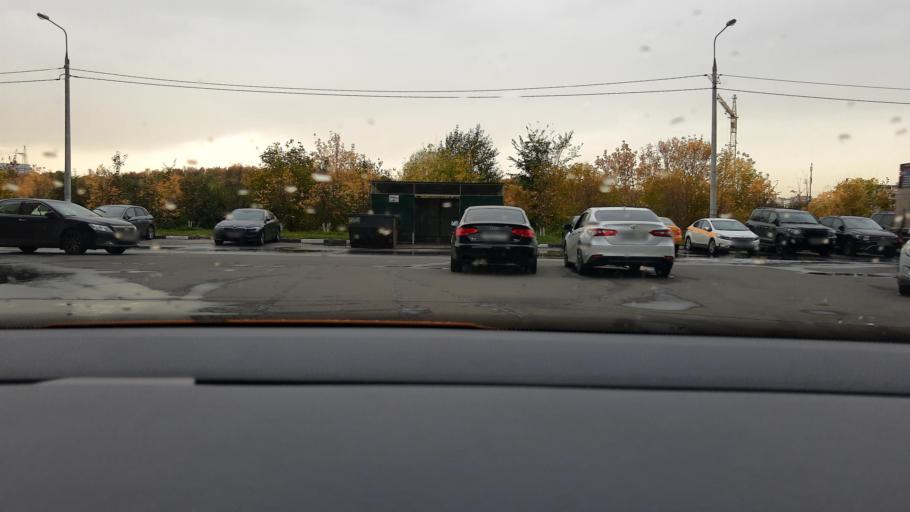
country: RU
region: Moscow
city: Ivanovskoye
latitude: 55.7732
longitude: 37.8464
